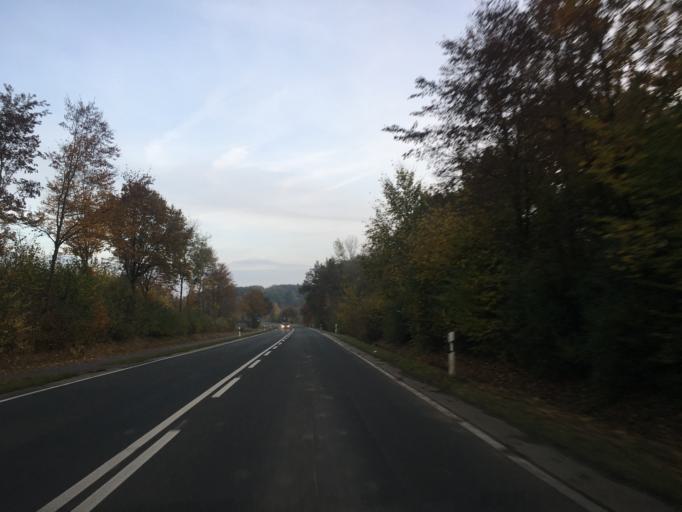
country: DE
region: North Rhine-Westphalia
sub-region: Regierungsbezirk Munster
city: Altenberge
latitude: 52.0605
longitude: 7.4521
